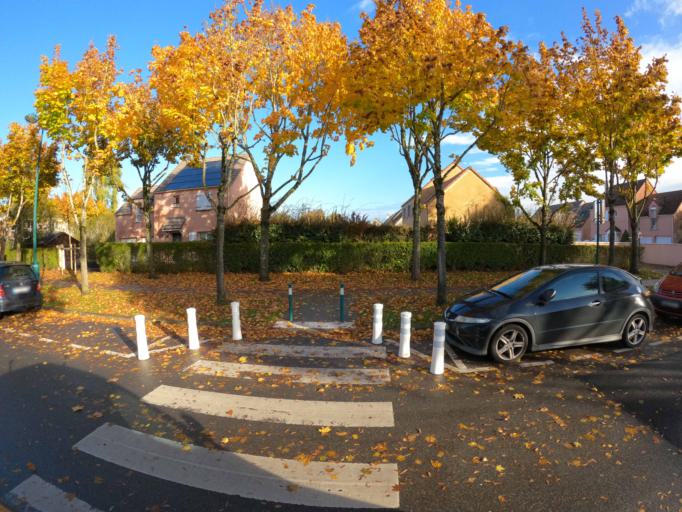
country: FR
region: Ile-de-France
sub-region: Departement de Seine-et-Marne
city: Bailly-Romainvilliers
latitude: 48.8437
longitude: 2.8206
